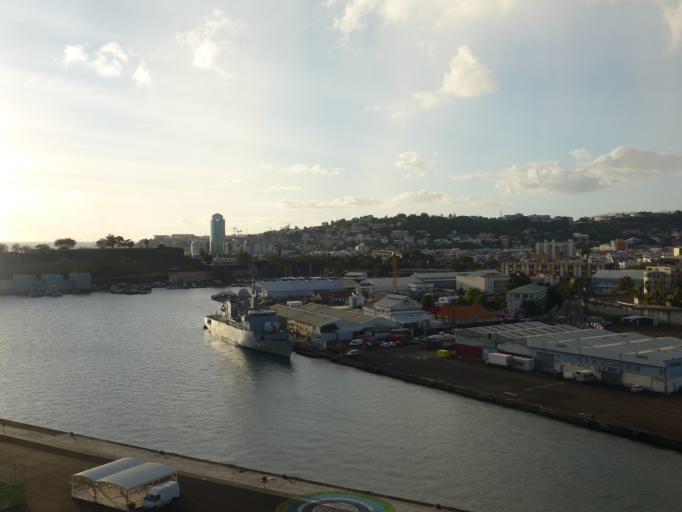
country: MQ
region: Martinique
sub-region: Martinique
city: Fort-de-France
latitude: 14.6014
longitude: -61.0601
